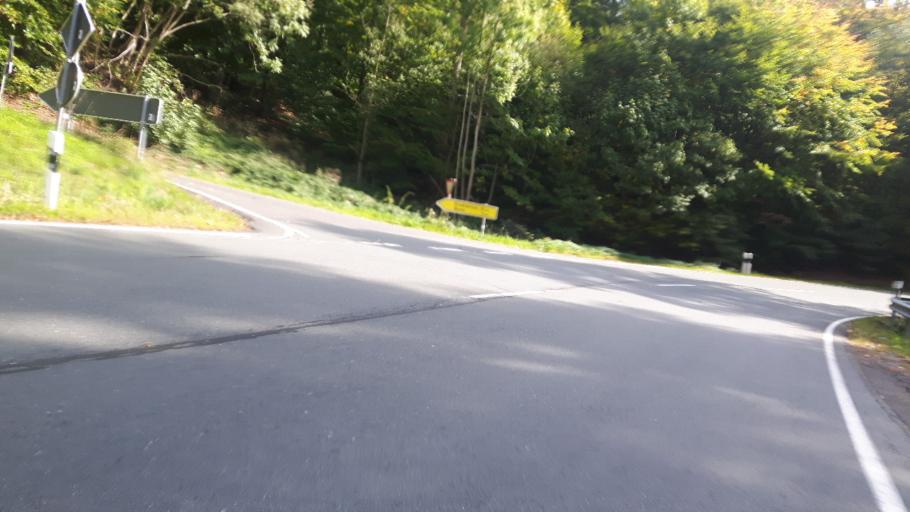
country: DE
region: North Rhine-Westphalia
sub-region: Regierungsbezirk Arnsberg
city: Erndtebruck
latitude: 50.9219
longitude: 8.2292
